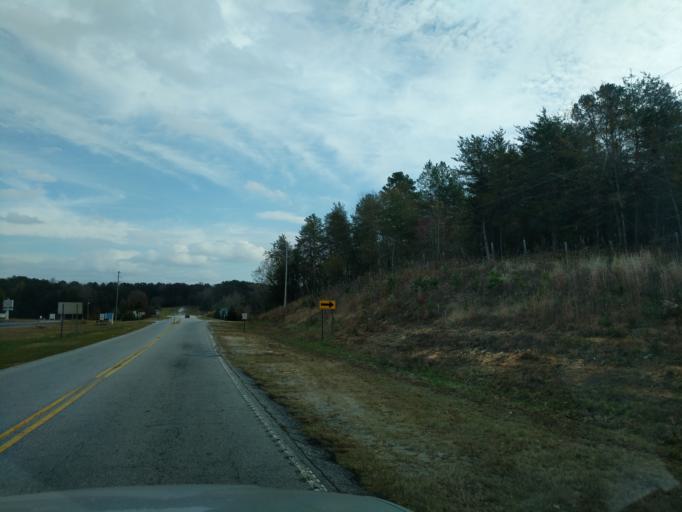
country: US
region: Georgia
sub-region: Franklin County
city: Gumlog
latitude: 34.4924
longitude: -83.0261
